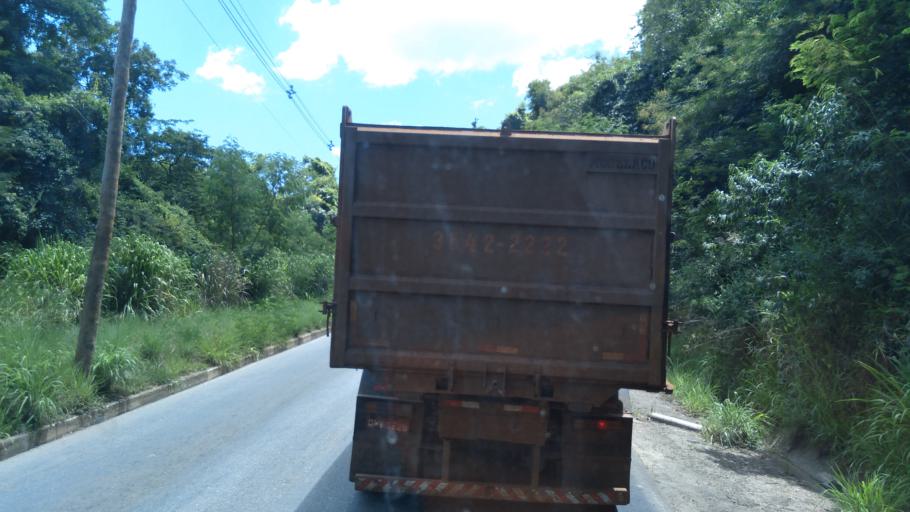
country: BR
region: Minas Gerais
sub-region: Santa Luzia
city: Santa Luzia
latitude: -19.8603
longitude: -43.8502
